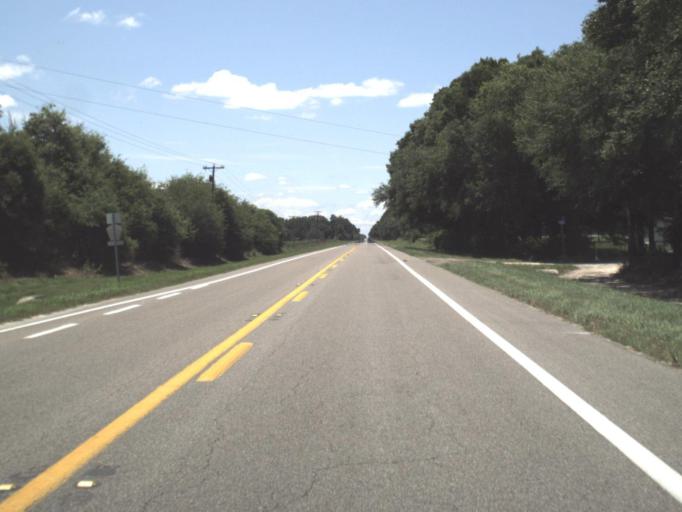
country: US
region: Florida
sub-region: Lafayette County
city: Mayo
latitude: 29.9846
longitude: -82.9997
